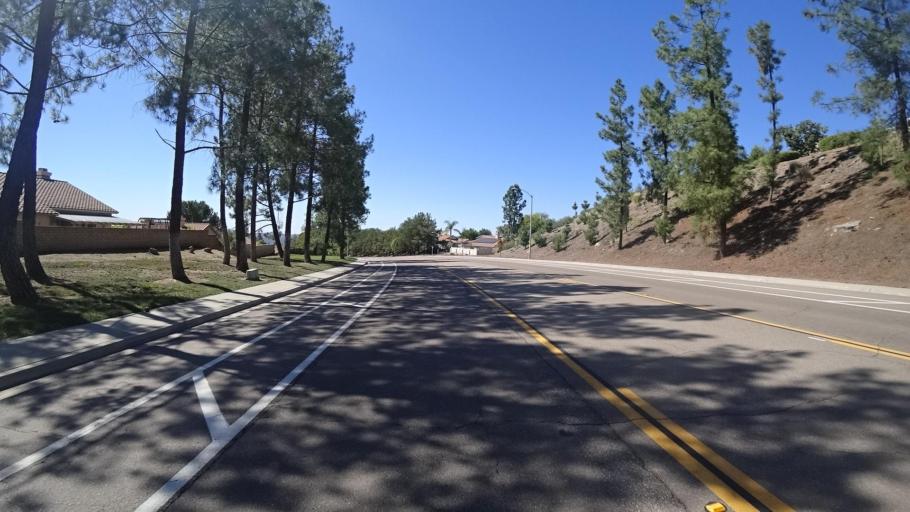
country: US
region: California
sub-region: San Diego County
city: Alpine
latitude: 32.8444
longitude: -116.7782
